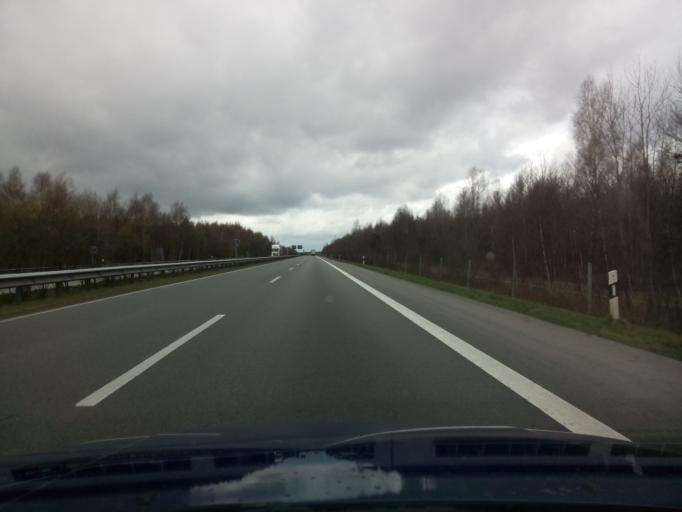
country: DE
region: Lower Saxony
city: Haren
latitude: 52.7215
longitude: 7.1580
